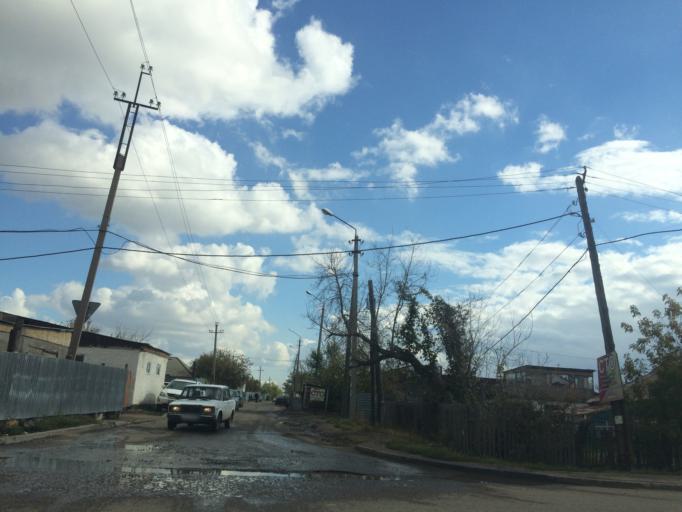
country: KZ
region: Astana Qalasy
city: Astana
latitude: 51.1864
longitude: 71.3826
